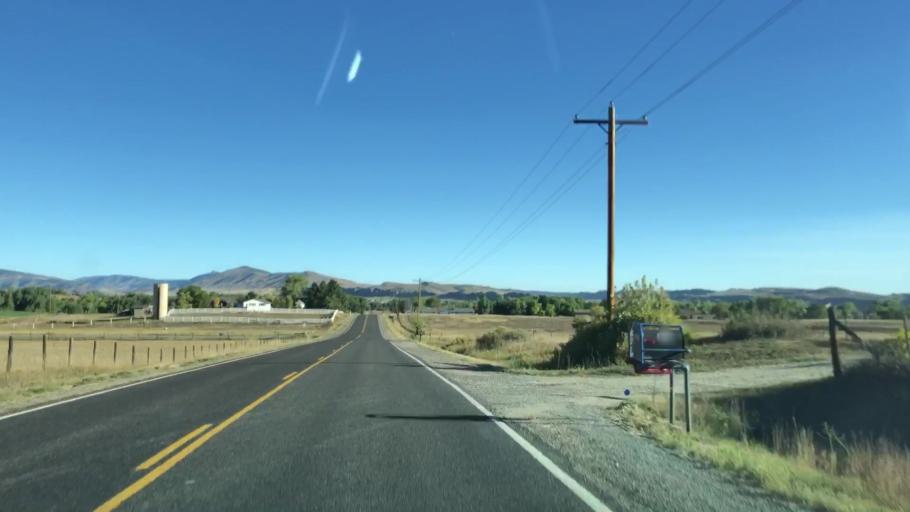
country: US
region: Colorado
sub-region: Larimer County
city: Loveland
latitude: 40.3866
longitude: -105.1633
